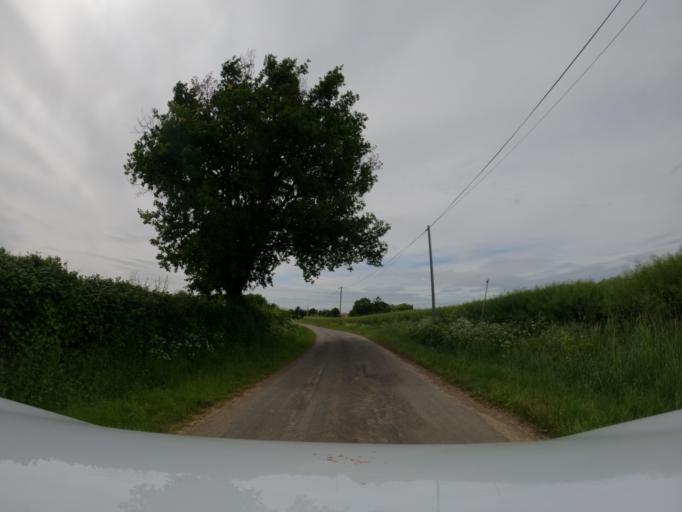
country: FR
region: Pays de la Loire
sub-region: Departement de la Vendee
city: Saint-Hilaire-des-Loges
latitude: 46.5009
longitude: -0.6370
